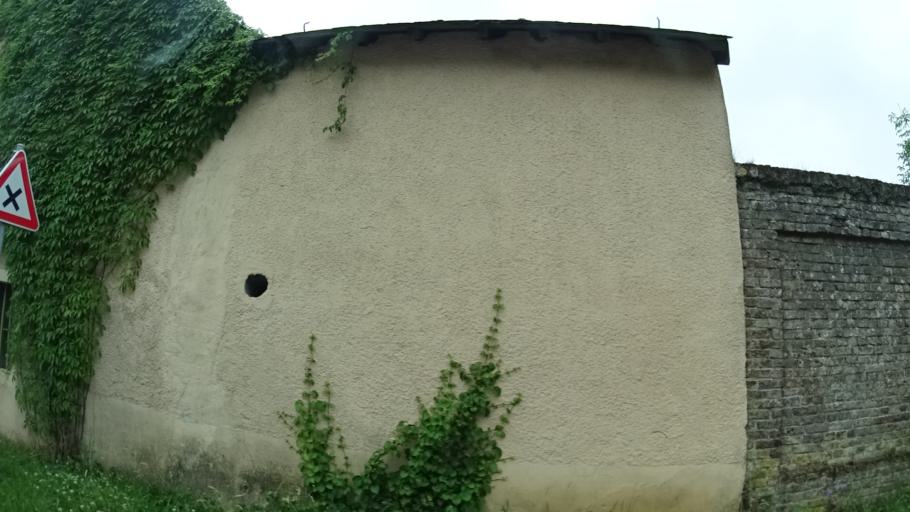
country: LU
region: Luxembourg
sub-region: Canton de Capellen
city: Steinfort
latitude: 49.6477
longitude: 5.8907
